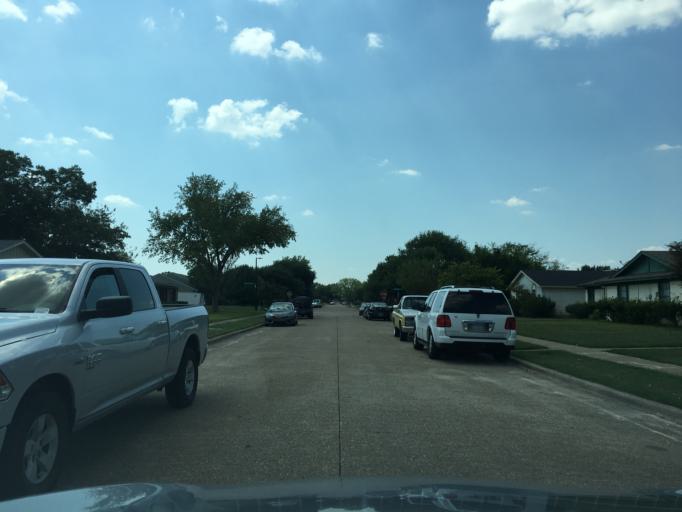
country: US
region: Texas
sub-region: Dallas County
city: Garland
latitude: 32.9483
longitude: -96.6586
